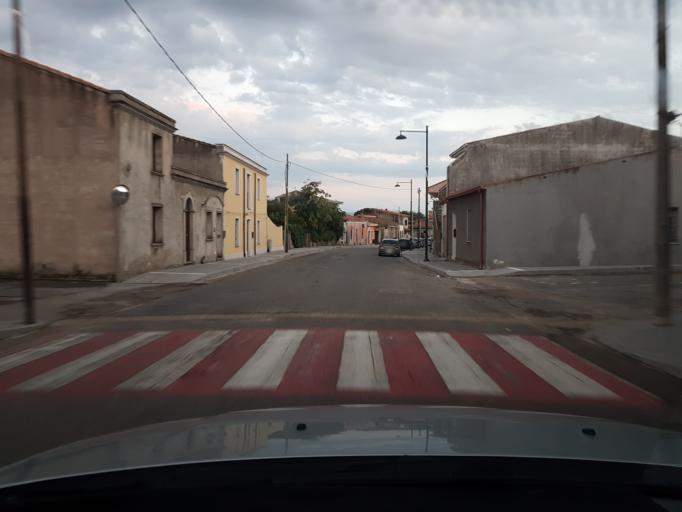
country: IT
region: Sardinia
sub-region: Provincia di Oristano
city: Tramatza
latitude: 40.0023
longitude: 8.6491
